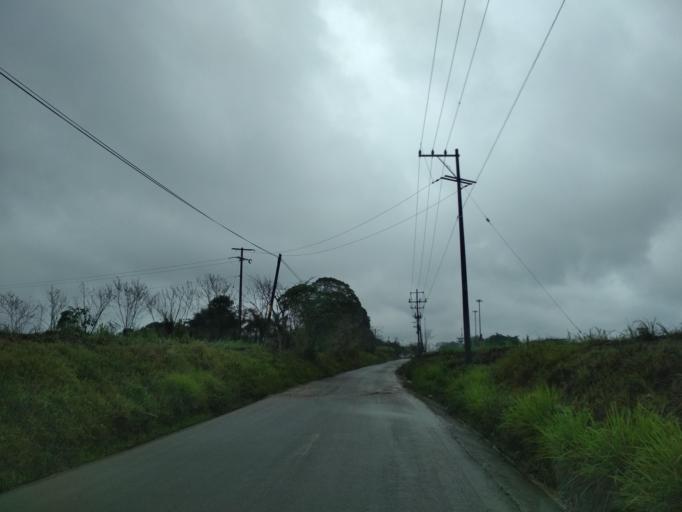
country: MX
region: Veracruz
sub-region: Amatlan de los Reyes
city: Centro de Readaptacion Social
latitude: 18.8357
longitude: -96.9382
